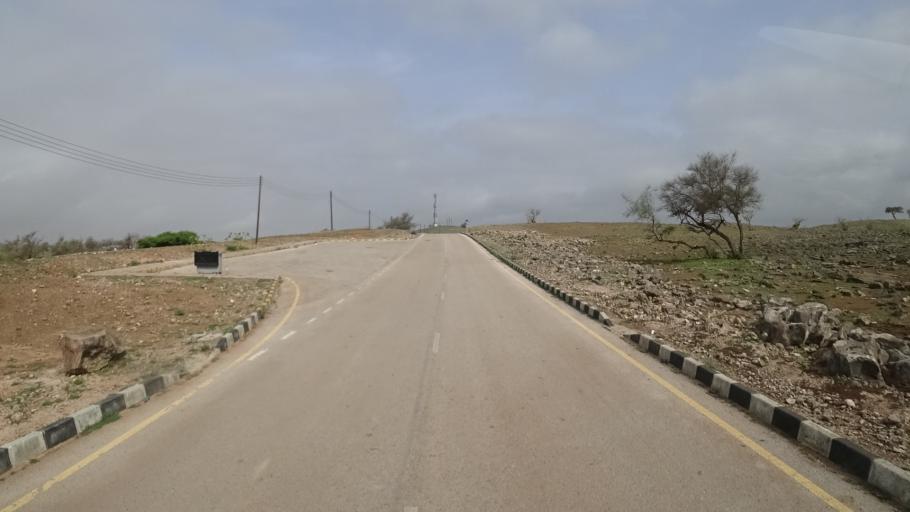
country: OM
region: Zufar
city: Salalah
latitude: 17.0774
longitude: 54.4495
